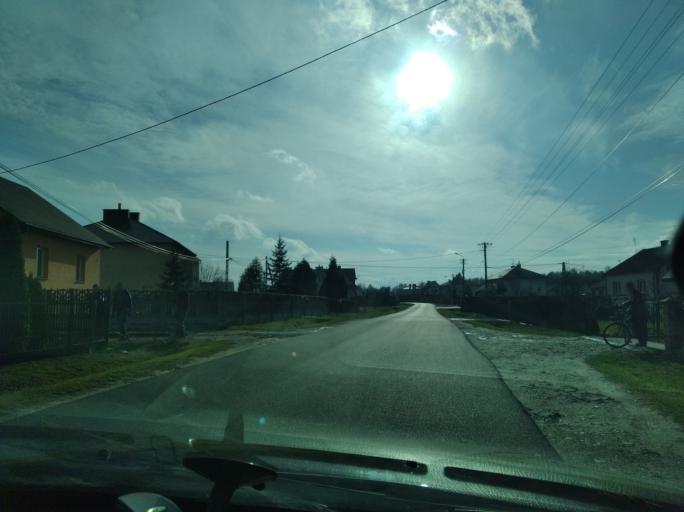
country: PL
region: Subcarpathian Voivodeship
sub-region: Powiat ropczycko-sedziszowski
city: Sedziszow Malopolski
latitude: 50.1065
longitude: 21.7333
